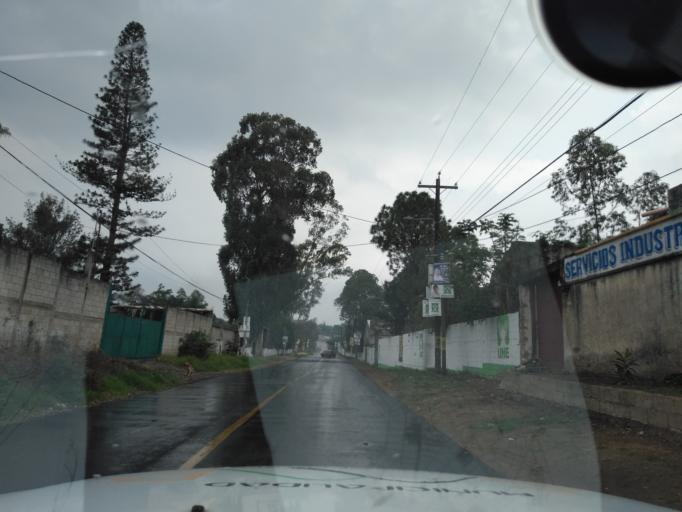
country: GT
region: Guatemala
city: Petapa
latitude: 14.5053
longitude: -90.5536
